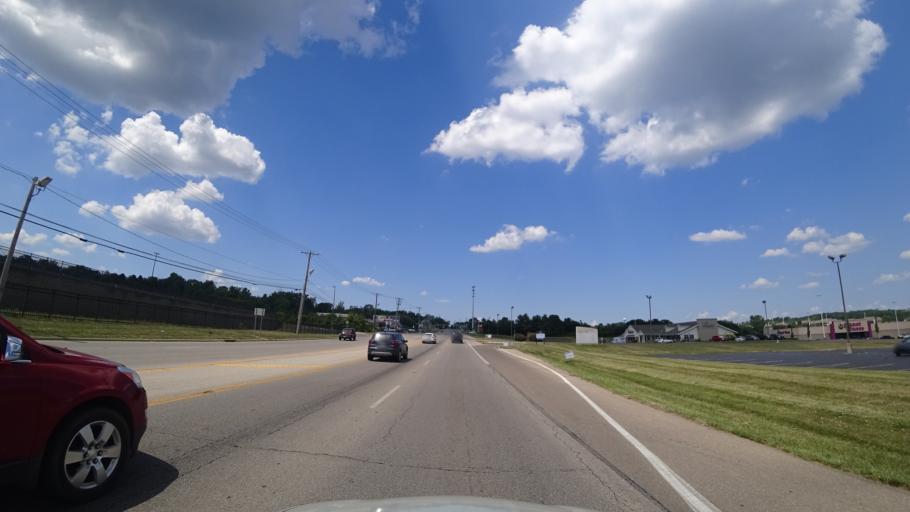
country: US
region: Ohio
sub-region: Butler County
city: Hamilton
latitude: 39.4265
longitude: -84.5969
